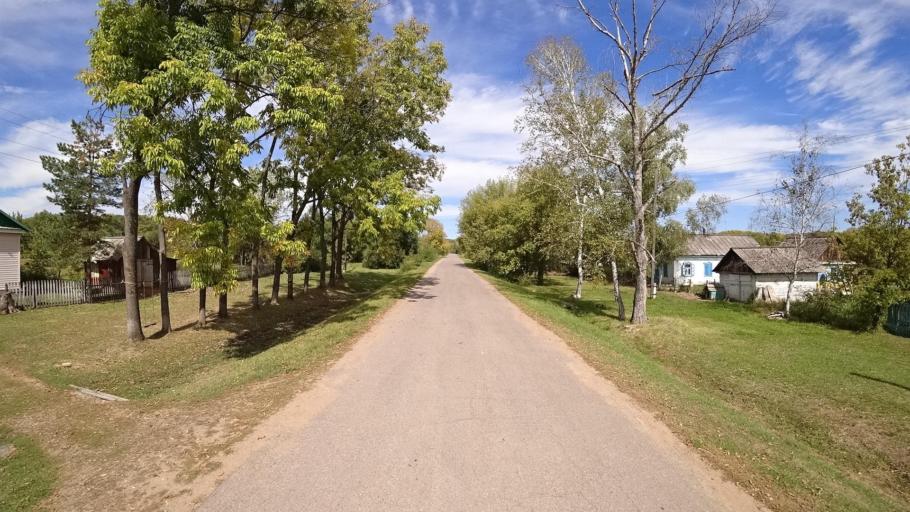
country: RU
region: Primorskiy
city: Yakovlevka
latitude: 44.6466
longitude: 133.5967
